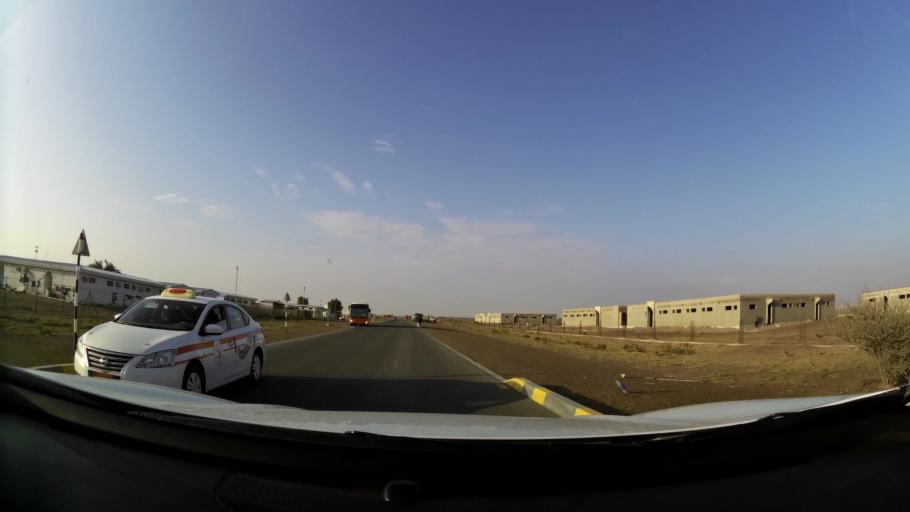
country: AE
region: Abu Dhabi
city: Al Ain
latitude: 24.1427
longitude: 55.8455
